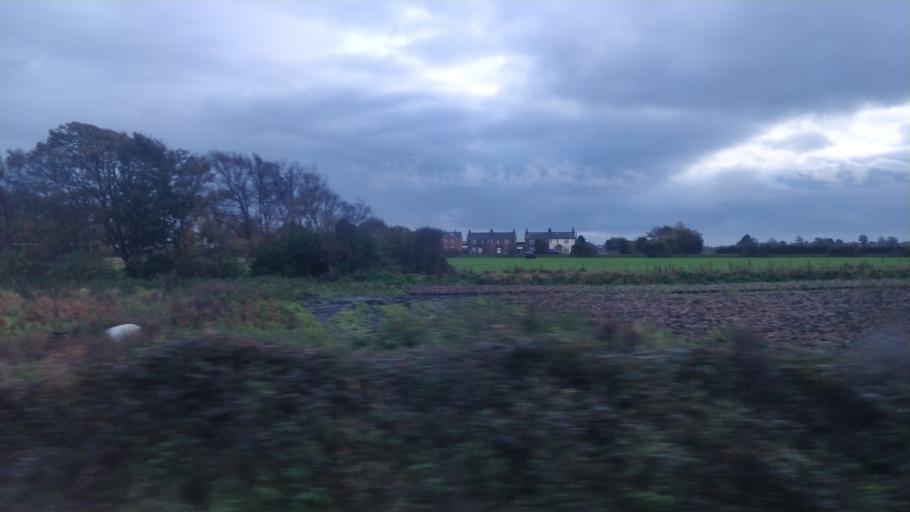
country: GB
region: England
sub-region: Lancashire
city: Banks
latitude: 53.6251
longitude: -2.9191
